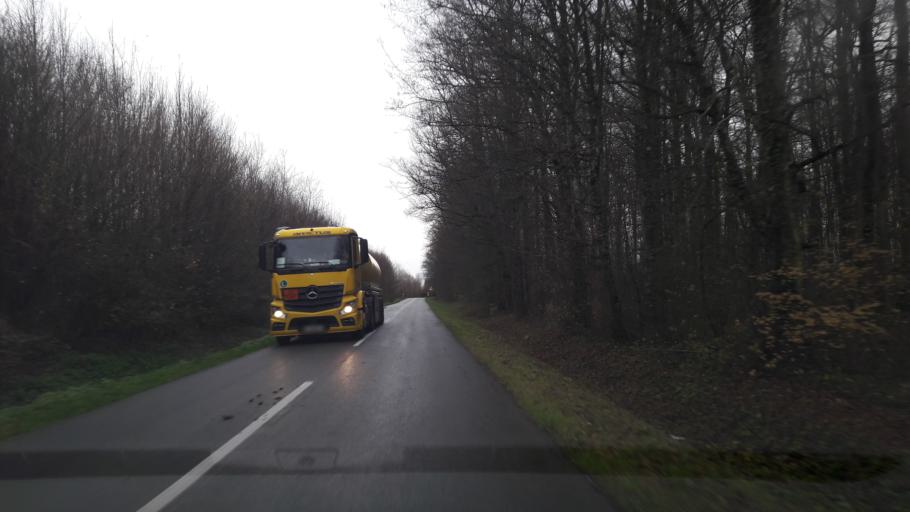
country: HR
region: Osjecko-Baranjska
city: Velimirovac
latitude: 45.6294
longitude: 18.1002
